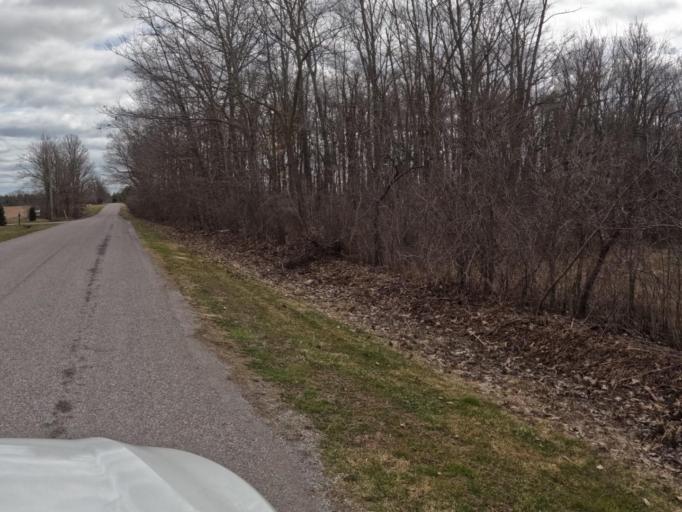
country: CA
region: Ontario
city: Norfolk County
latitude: 42.8496
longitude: -80.1699
